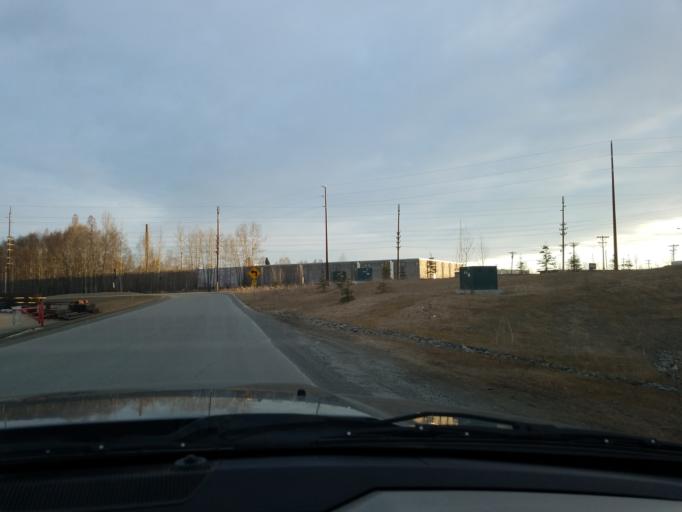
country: US
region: Alaska
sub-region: Anchorage Municipality
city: Anchorage
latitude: 61.1653
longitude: -149.8998
